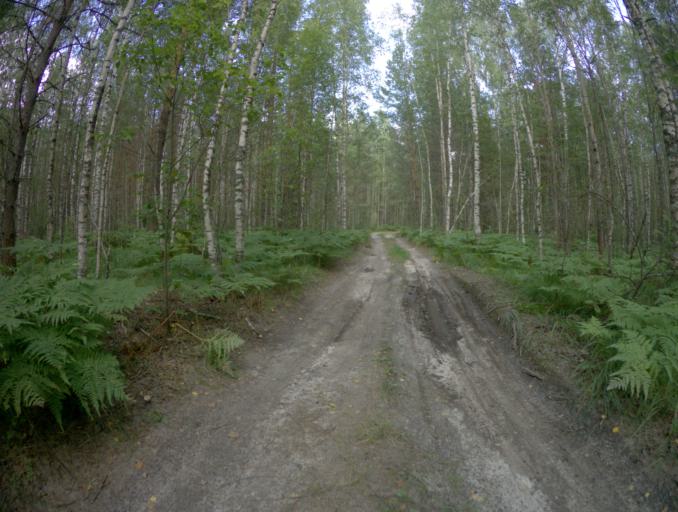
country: RU
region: Vladimir
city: Raduzhnyy
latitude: 55.9520
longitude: 40.1972
